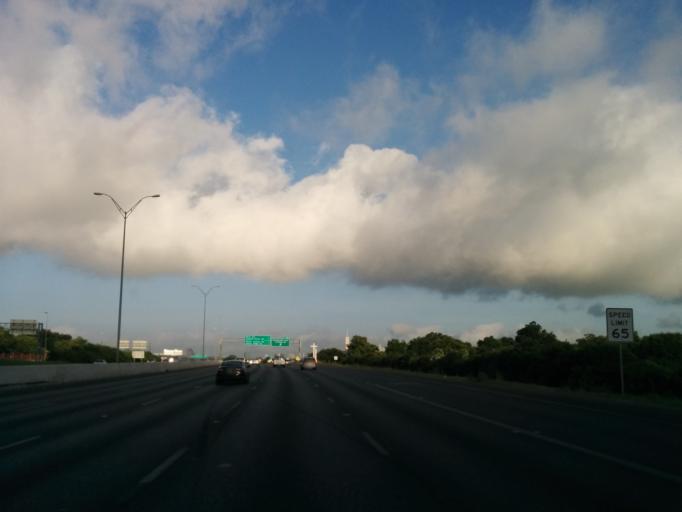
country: US
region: Texas
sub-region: Bexar County
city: Castle Hills
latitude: 29.5208
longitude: -98.5129
